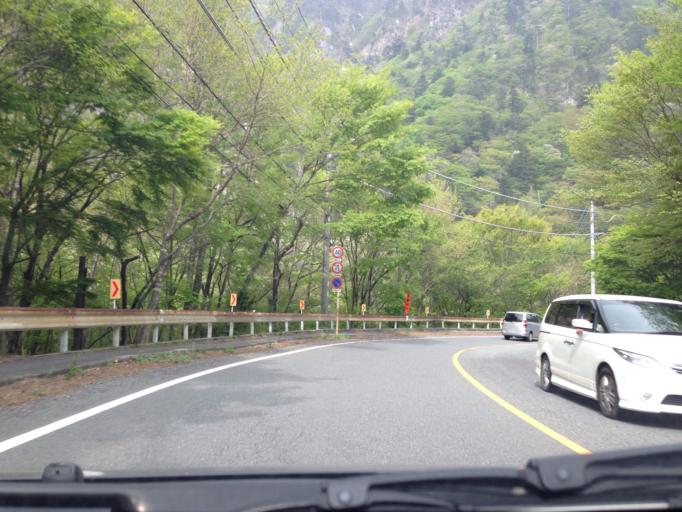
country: JP
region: Tochigi
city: Yaita
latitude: 36.9681
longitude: 139.8337
